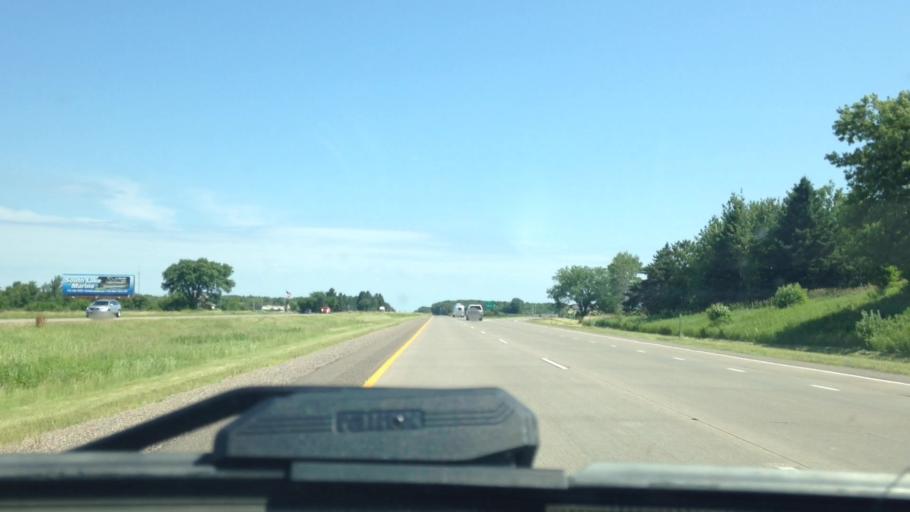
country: US
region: Wisconsin
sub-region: Barron County
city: Rice Lake
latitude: 45.5030
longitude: -91.7633
